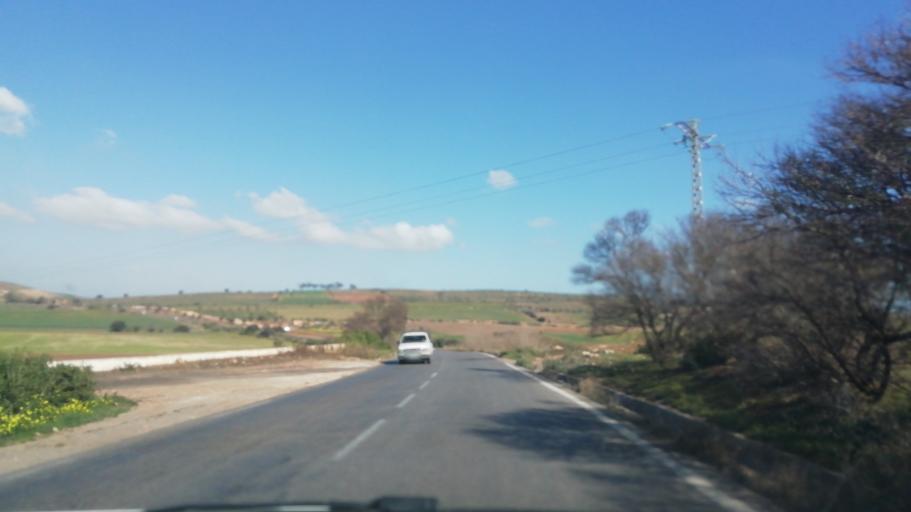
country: DZ
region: Oran
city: Ain el Bya
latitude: 35.7339
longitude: -0.2526
